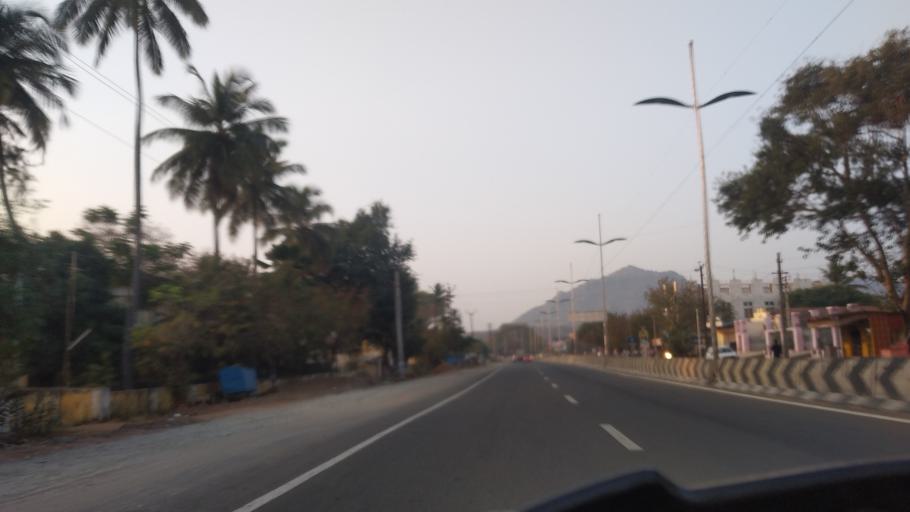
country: IN
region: Tamil Nadu
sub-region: Coimbatore
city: Madukkarai
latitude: 10.9348
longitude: 76.9505
